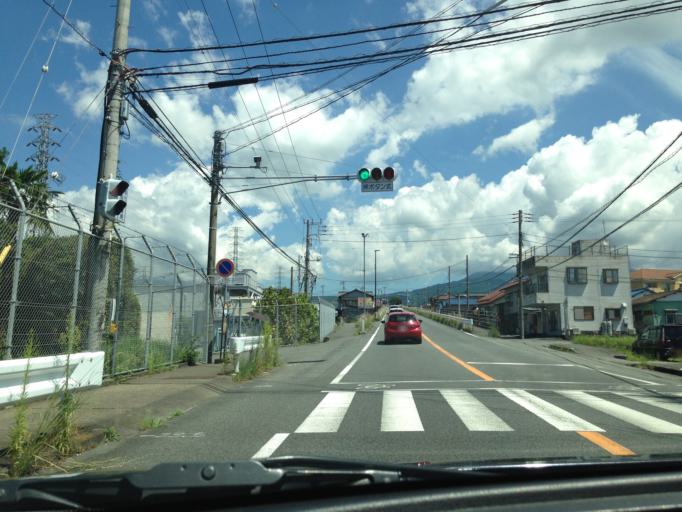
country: JP
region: Shizuoka
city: Fuji
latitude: 35.1750
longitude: 138.6927
